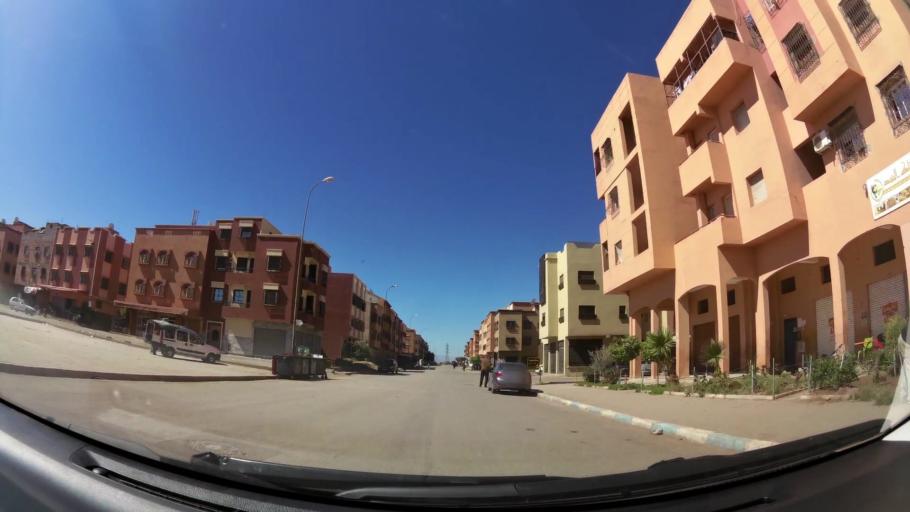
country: MA
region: Marrakech-Tensift-Al Haouz
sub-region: Marrakech
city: Marrakesh
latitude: 31.5728
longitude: -8.0560
